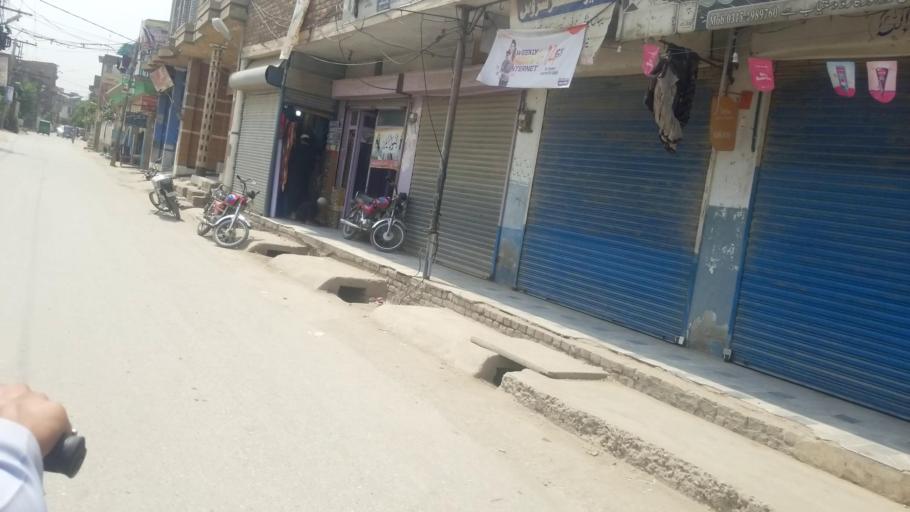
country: PK
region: Khyber Pakhtunkhwa
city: Peshawar
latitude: 34.0267
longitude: 71.5884
